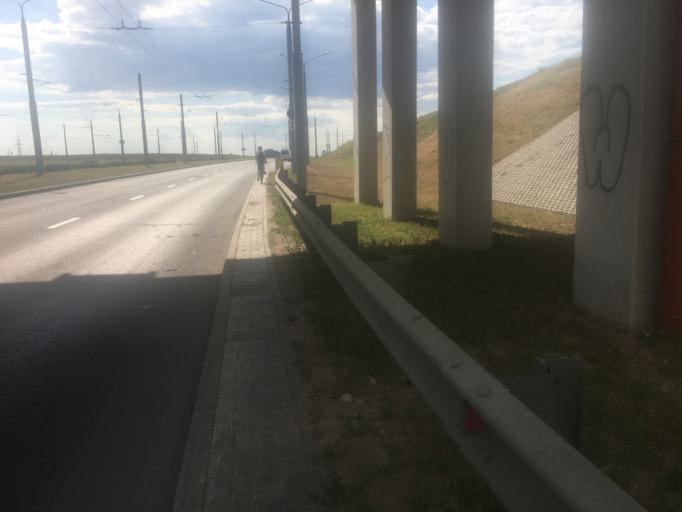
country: BY
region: Grodnenskaya
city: Hrodna
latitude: 53.6460
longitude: 23.8184
